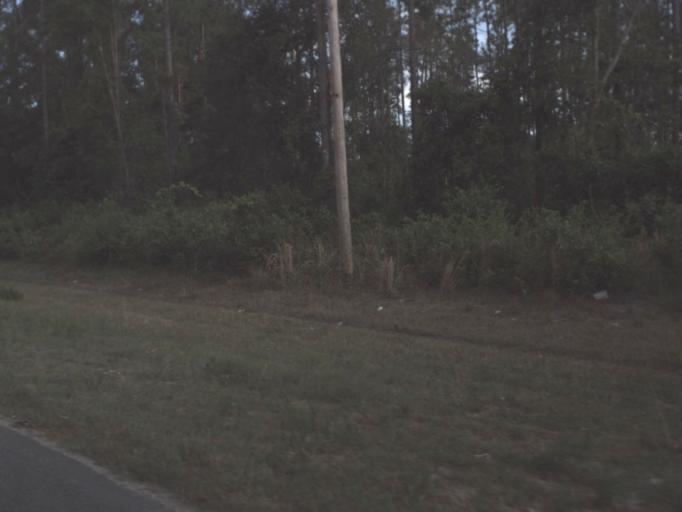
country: US
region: Florida
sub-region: Marion County
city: Silver Springs Shores
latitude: 29.1842
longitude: -81.8928
